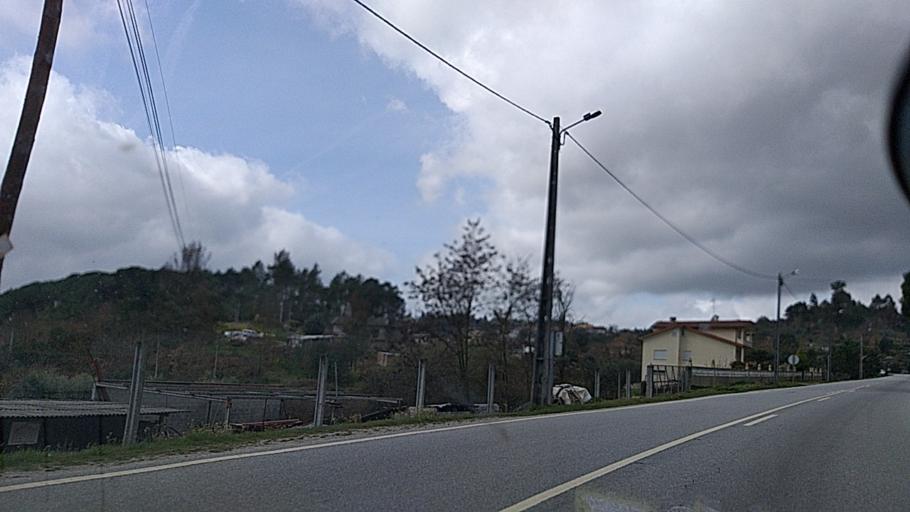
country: PT
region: Viseu
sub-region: Mangualde
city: Mangualde
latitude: 40.6324
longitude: -7.7426
